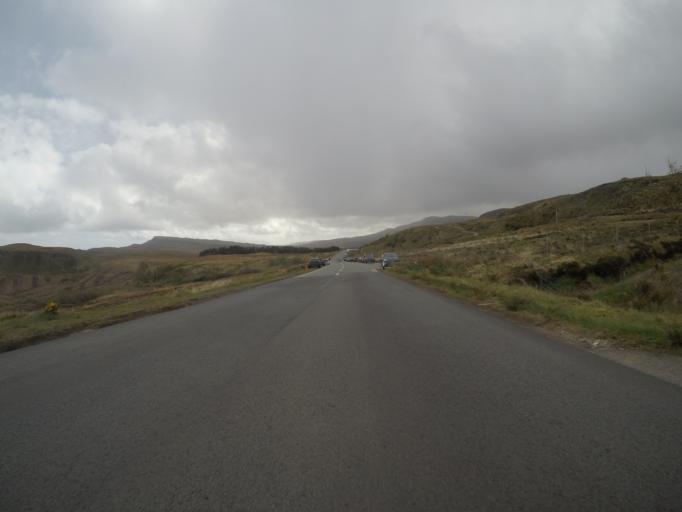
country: GB
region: Scotland
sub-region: Highland
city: Portree
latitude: 57.4999
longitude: -6.1568
